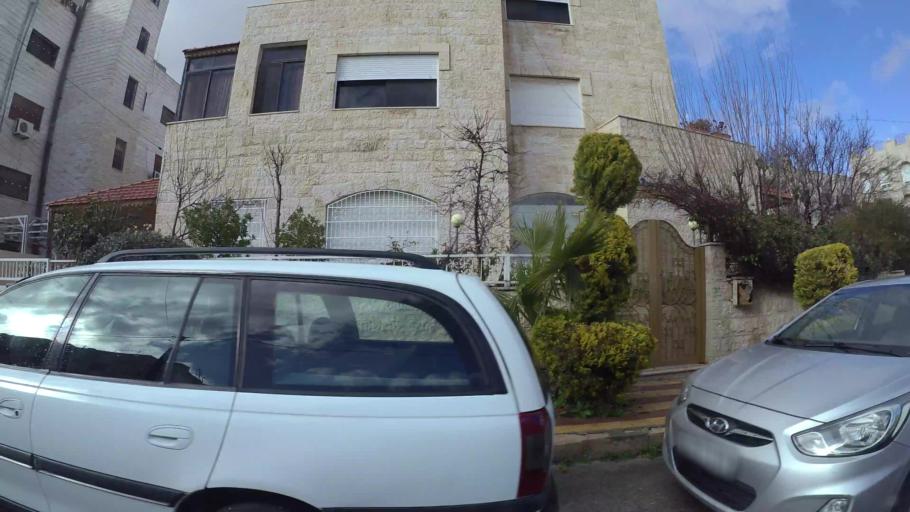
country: JO
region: Amman
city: Al Jubayhah
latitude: 32.0300
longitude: 35.8667
